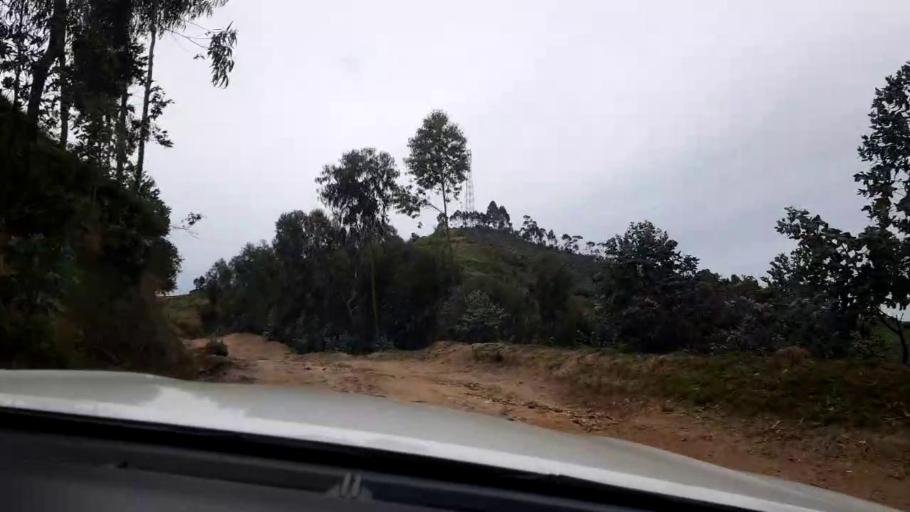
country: RW
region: Western Province
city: Kibuye
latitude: -1.8887
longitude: 29.4529
